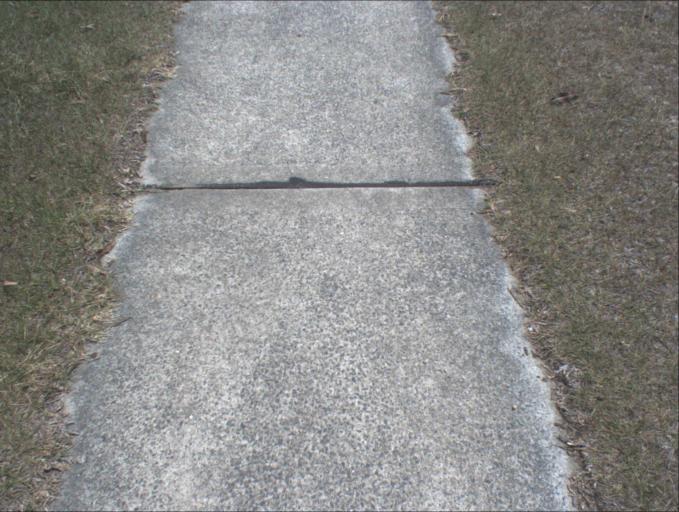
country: AU
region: Queensland
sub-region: Logan
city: Waterford West
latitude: -27.6988
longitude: 153.1644
